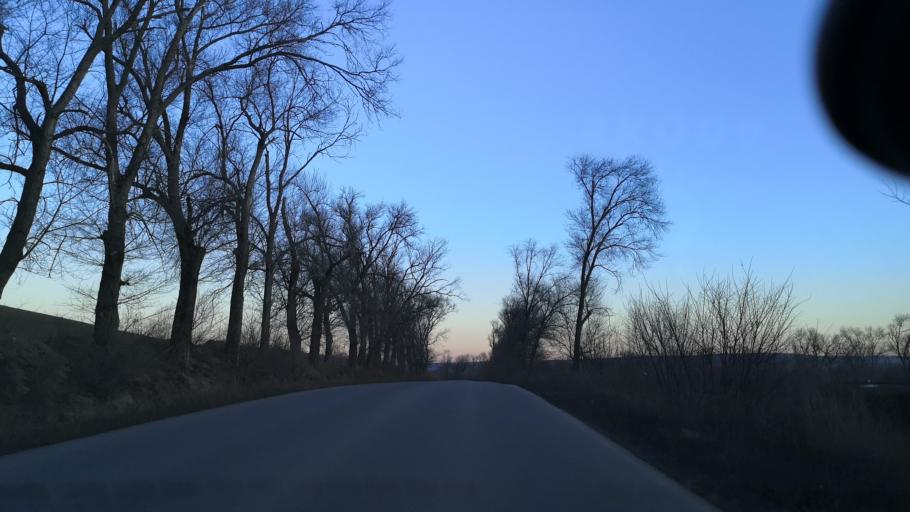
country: MD
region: Anenii Noi
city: Anenii Noi
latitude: 46.8901
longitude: 29.2455
